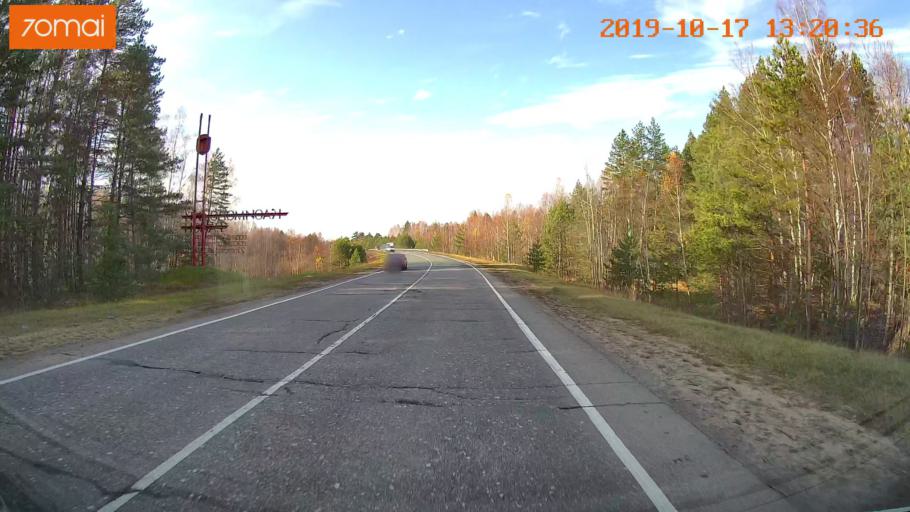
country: RU
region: Rjazan
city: Gus'-Zheleznyy
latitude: 55.0772
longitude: 41.0469
